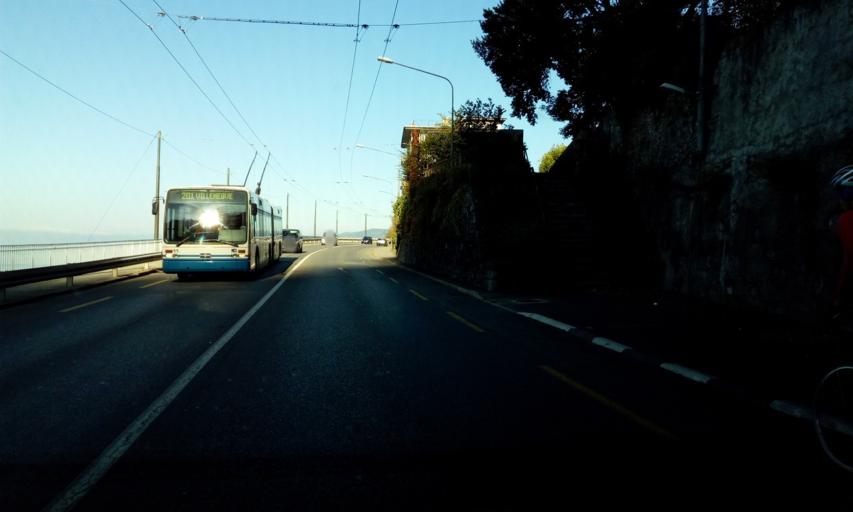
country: CH
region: Vaud
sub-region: Riviera-Pays-d'Enhaut District
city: Caux
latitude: 46.4192
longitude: 6.9278
